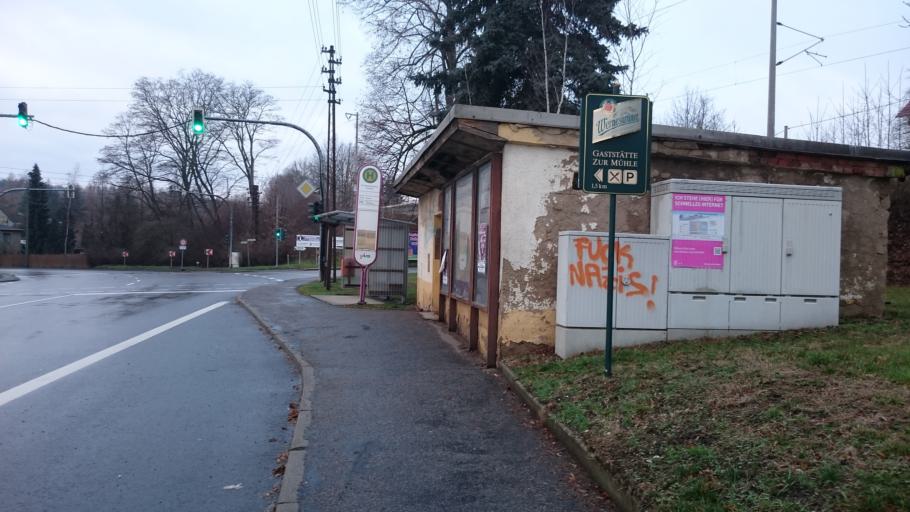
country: DE
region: Saxony
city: Dennheritz
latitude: 50.8165
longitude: 12.4928
